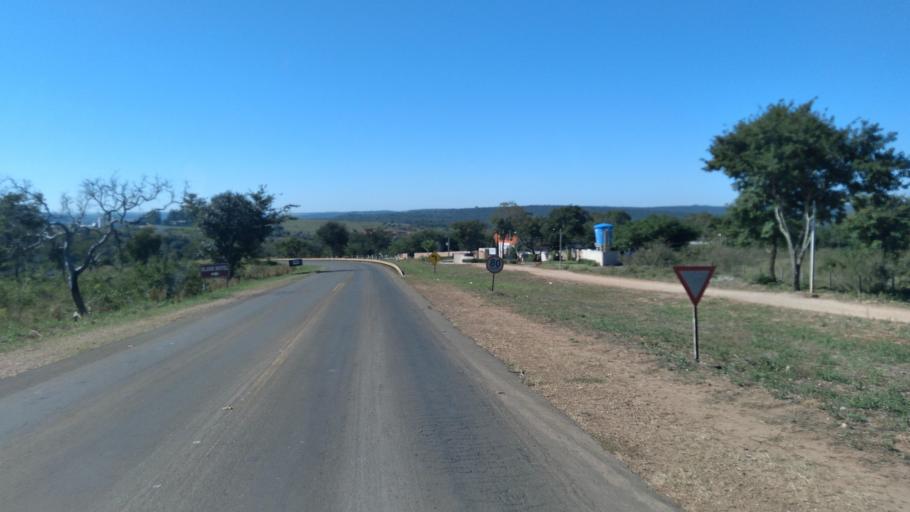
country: BR
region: Goias
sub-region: Mineiros
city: Mineiros
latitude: -17.5803
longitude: -52.5278
